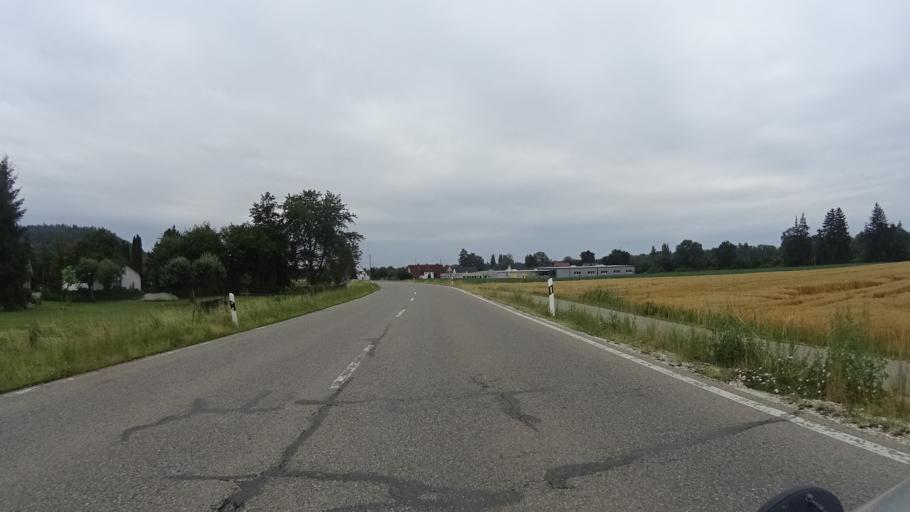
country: DE
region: Bavaria
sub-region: Swabia
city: Altenstadt
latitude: 48.1427
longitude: 10.1188
